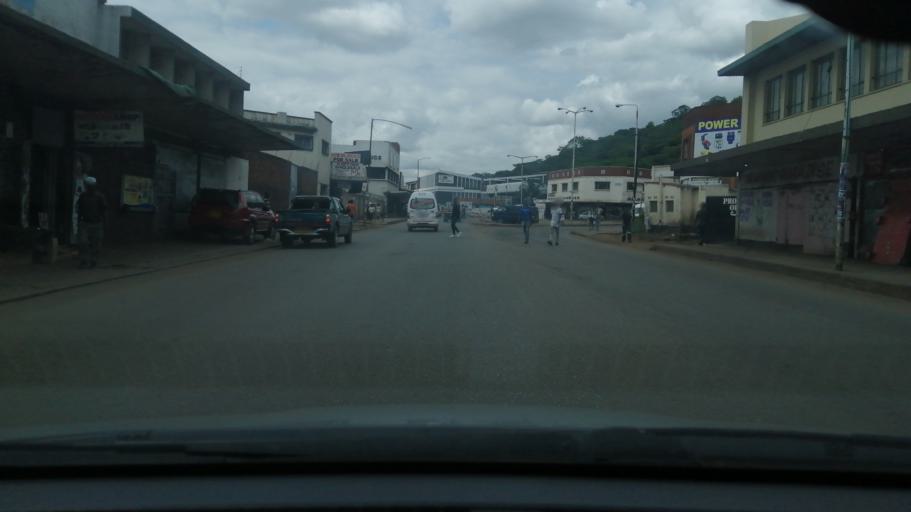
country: ZW
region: Harare
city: Harare
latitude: -17.8408
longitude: 31.0412
